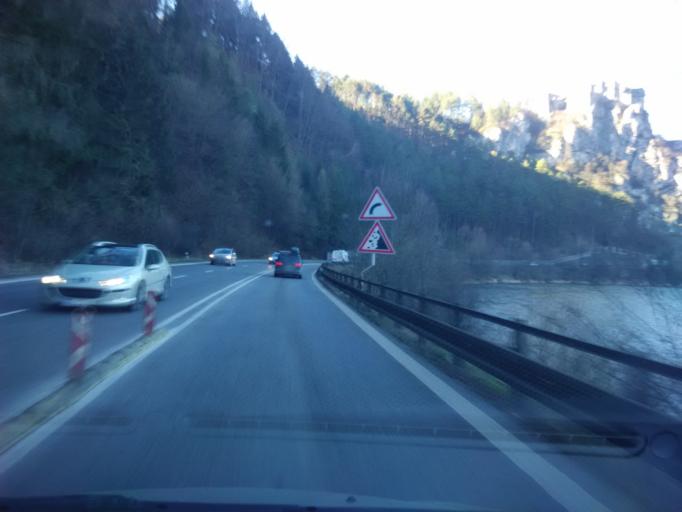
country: SK
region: Zilinsky
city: Krasnany
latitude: 49.1717
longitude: 18.8648
